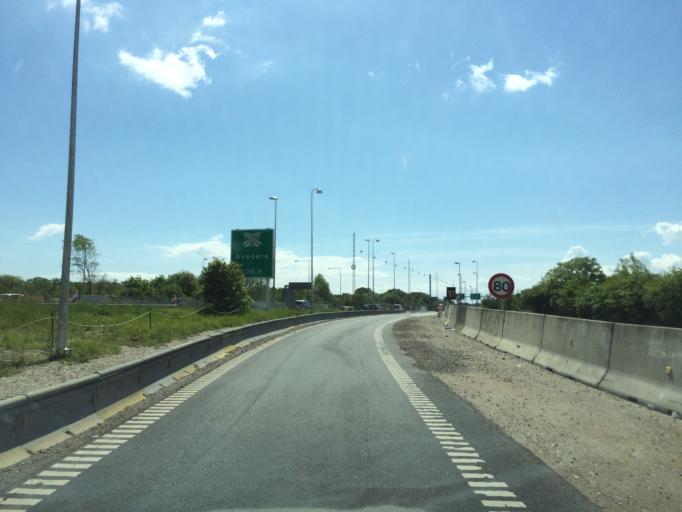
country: DK
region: Capital Region
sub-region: Brondby Kommune
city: Brondbyvester
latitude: 55.6397
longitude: 12.4250
